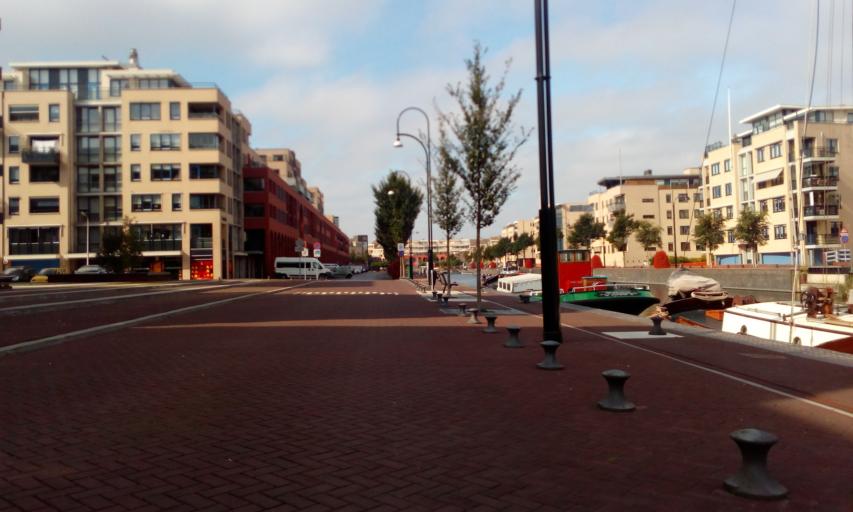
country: NL
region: South Holland
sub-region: Gemeente Katwijk
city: Katwijk aan Zee
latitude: 52.2051
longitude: 4.4039
